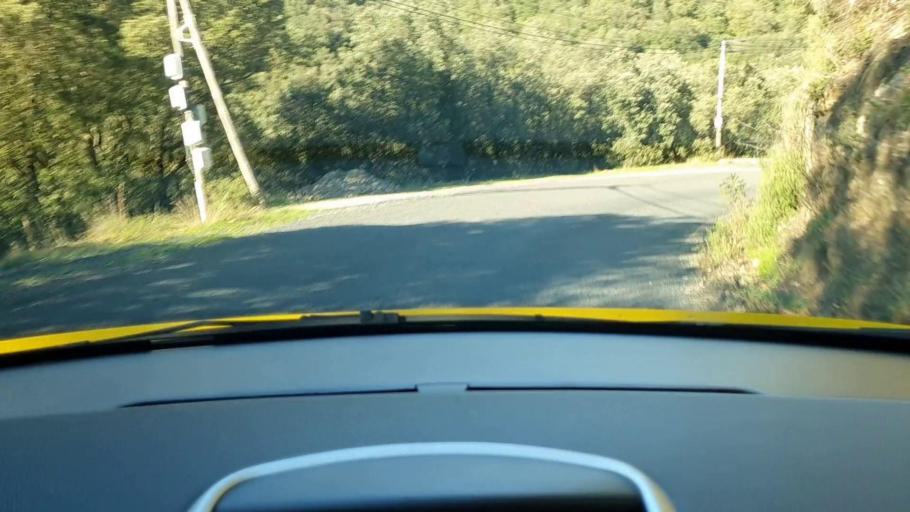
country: FR
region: Languedoc-Roussillon
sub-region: Departement du Gard
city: Sumene
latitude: 44.0186
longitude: 3.7237
